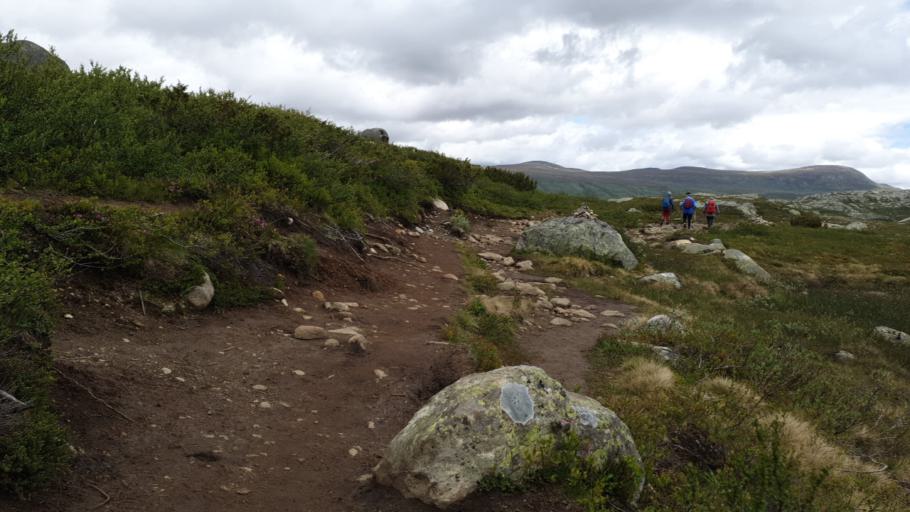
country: NO
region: Oppland
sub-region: Vestre Slidre
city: Slidre
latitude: 61.3149
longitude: 8.7999
